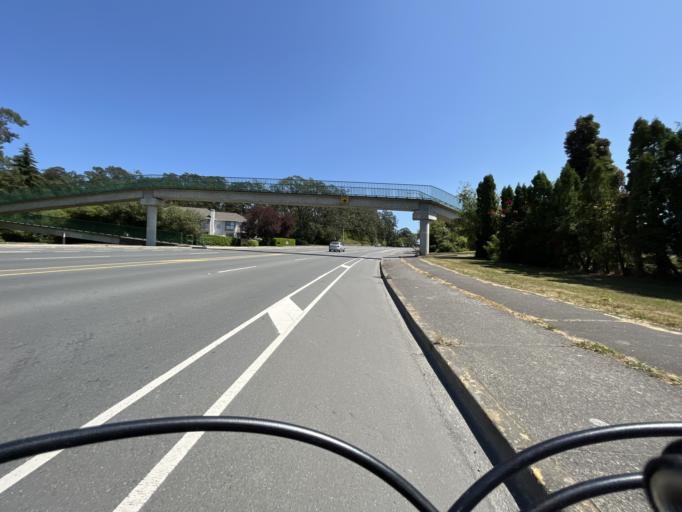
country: CA
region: British Columbia
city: Victoria
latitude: 48.4714
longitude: -123.3446
